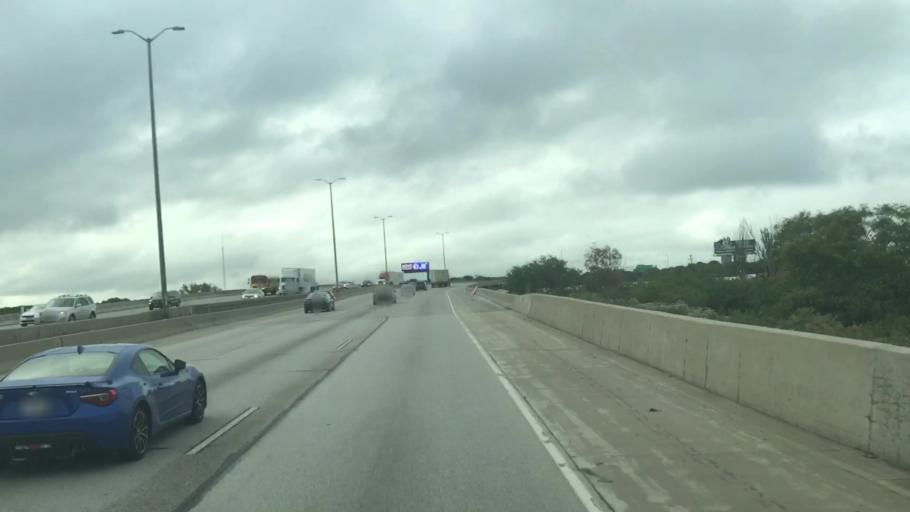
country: US
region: Wisconsin
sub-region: Milwaukee County
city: Saint Francis
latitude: 42.9894
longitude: -87.9146
